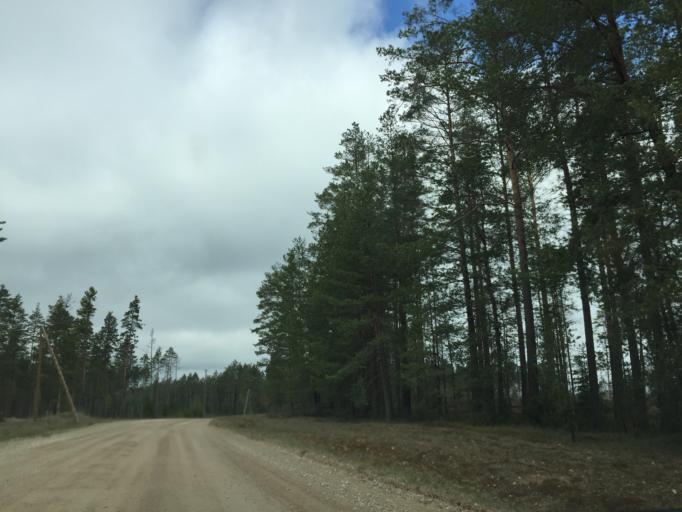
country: EE
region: Valgamaa
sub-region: Valga linn
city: Valga
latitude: 57.6473
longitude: 26.2221
